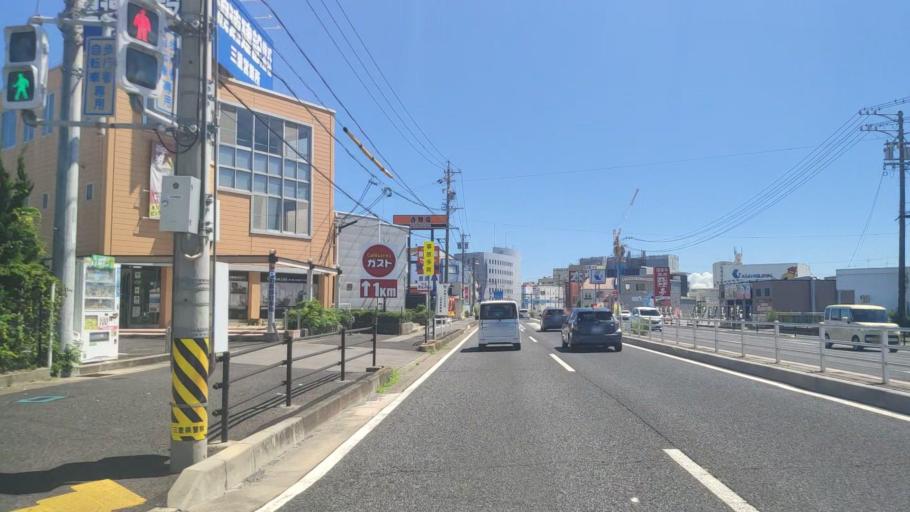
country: JP
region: Mie
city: Suzuka
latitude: 34.8390
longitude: 136.5883
